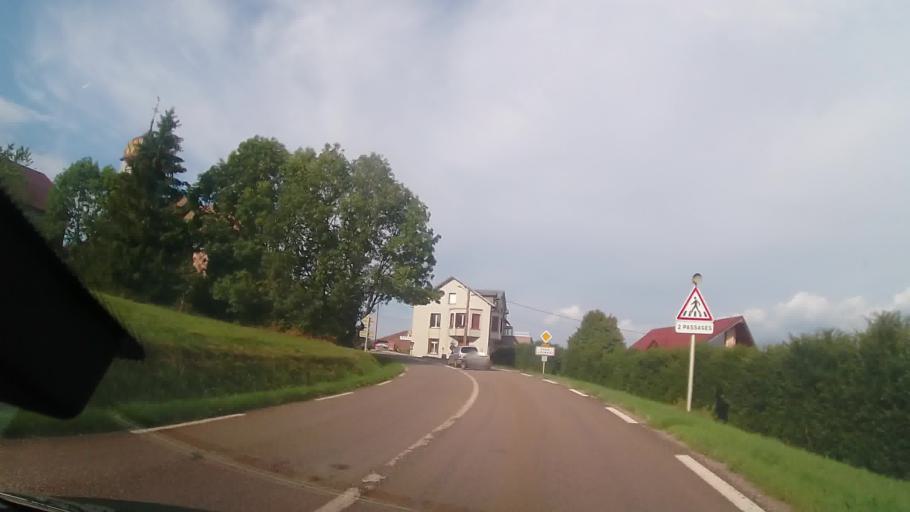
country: FR
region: Franche-Comte
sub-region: Departement du Jura
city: Morbier
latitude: 46.6035
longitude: 5.9037
